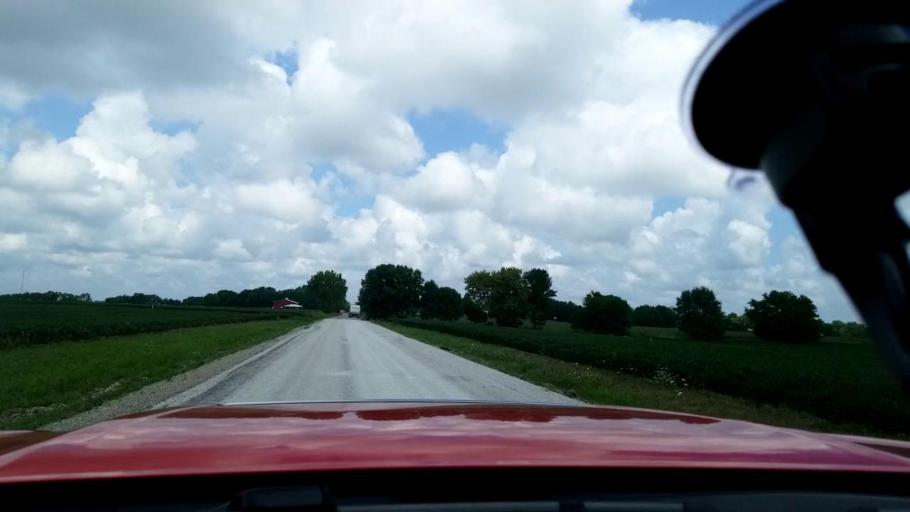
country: US
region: Iowa
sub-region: Decatur County
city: Lamoni
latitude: 40.7022
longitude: -94.0531
